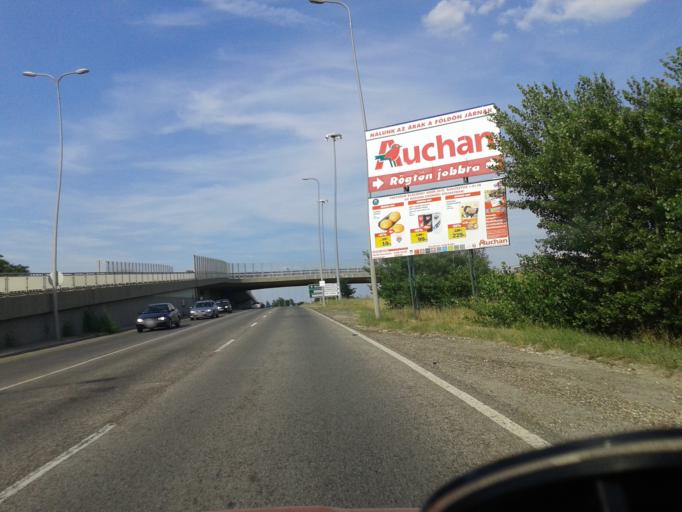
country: HU
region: Pest
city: Kistarcsa
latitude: 47.5378
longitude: 19.2475
